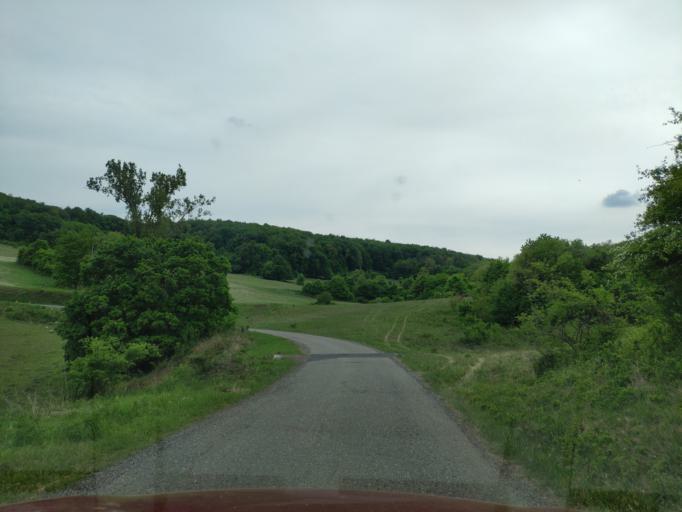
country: SK
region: Banskobystricky
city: Revuca
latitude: 48.5248
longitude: 20.1175
